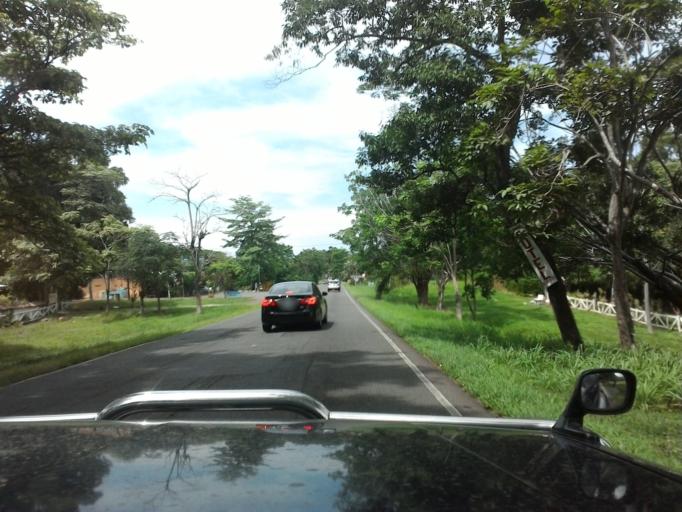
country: CR
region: Puntarenas
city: Esparza
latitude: 10.0094
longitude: -84.6186
